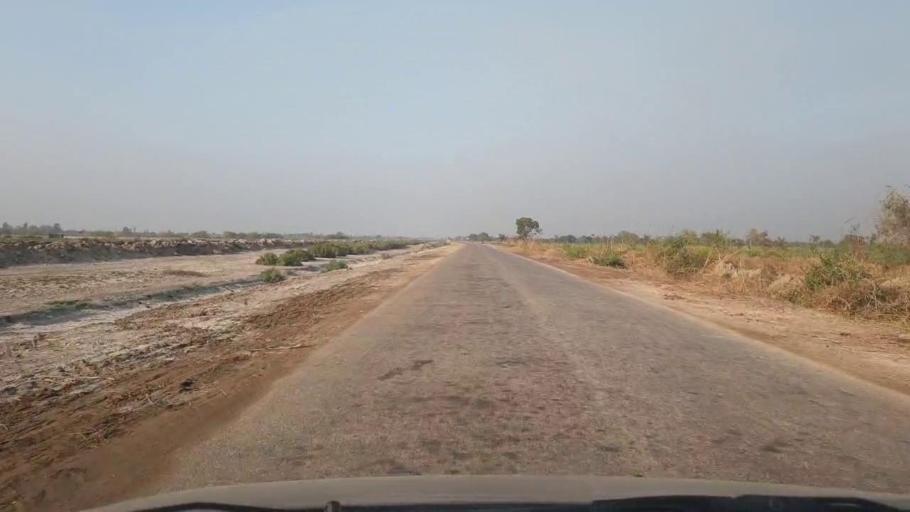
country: PK
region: Sindh
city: Mirwah Gorchani
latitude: 25.3519
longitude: 69.1730
